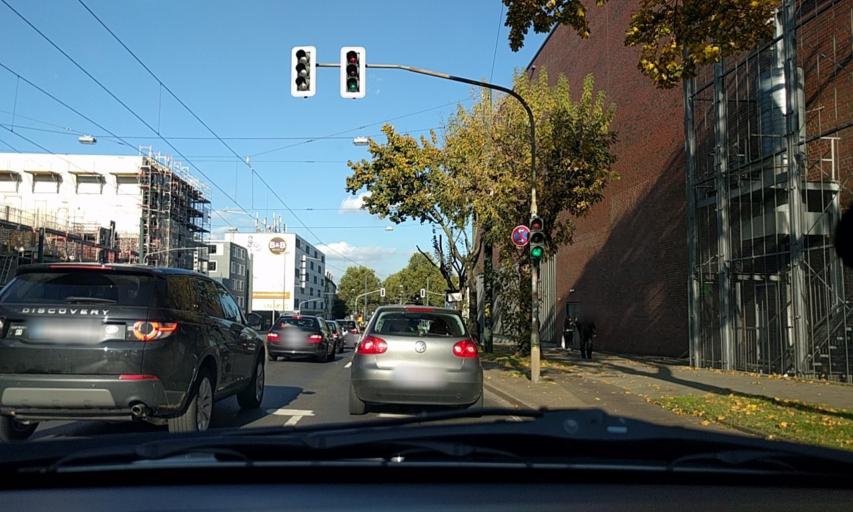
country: DE
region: North Rhine-Westphalia
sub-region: Regierungsbezirk Dusseldorf
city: Dusseldorf
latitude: 51.2201
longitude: 6.8081
